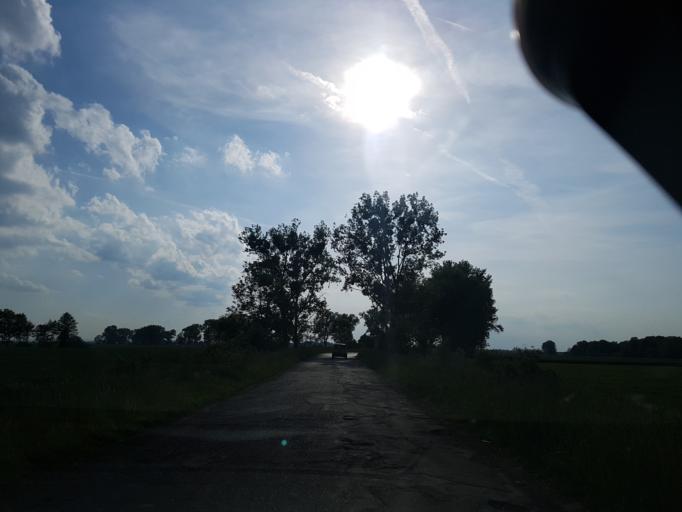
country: PL
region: Lower Silesian Voivodeship
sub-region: Powiat strzelinski
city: Wiazow
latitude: 50.8452
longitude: 17.2399
